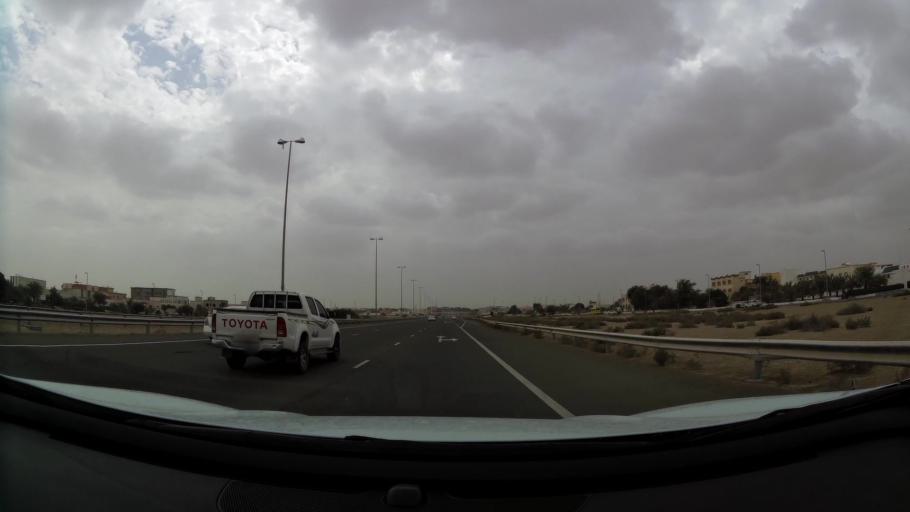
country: AE
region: Abu Dhabi
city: Abu Dhabi
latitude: 24.3316
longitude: 54.6397
